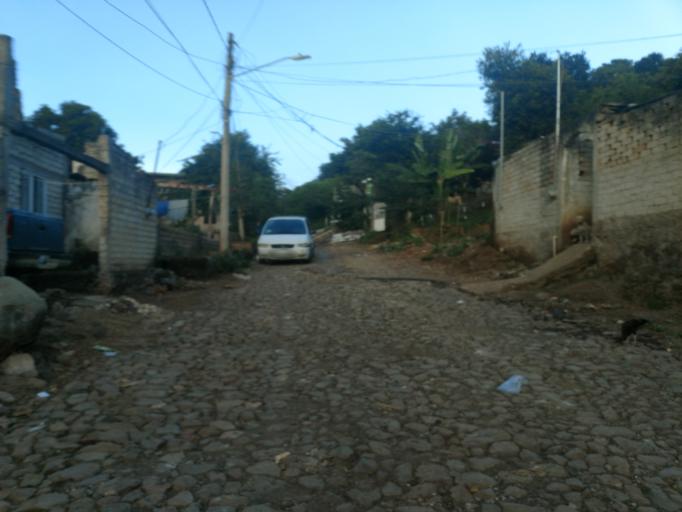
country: MX
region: Nayarit
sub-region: Tepic
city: La Corregidora
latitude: 21.4697
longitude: -104.7963
